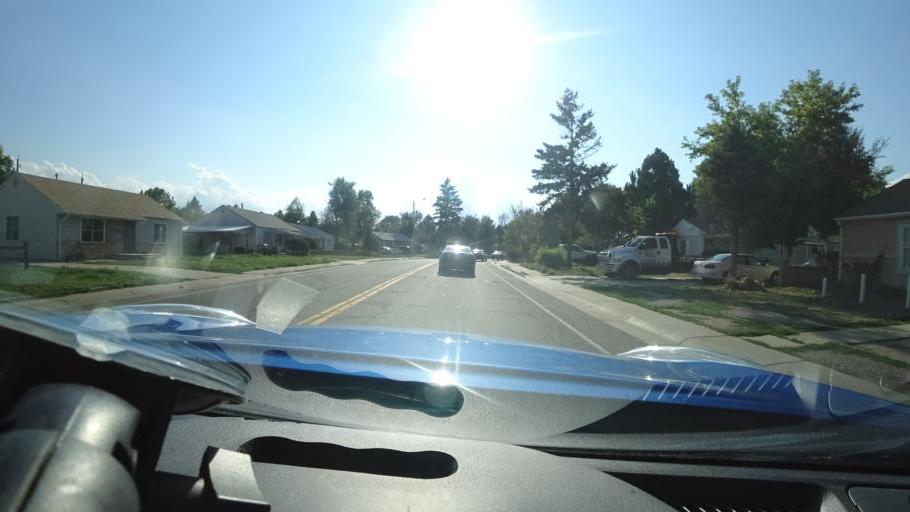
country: US
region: Colorado
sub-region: Arapahoe County
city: Sheridan
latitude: 39.6782
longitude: -105.0308
